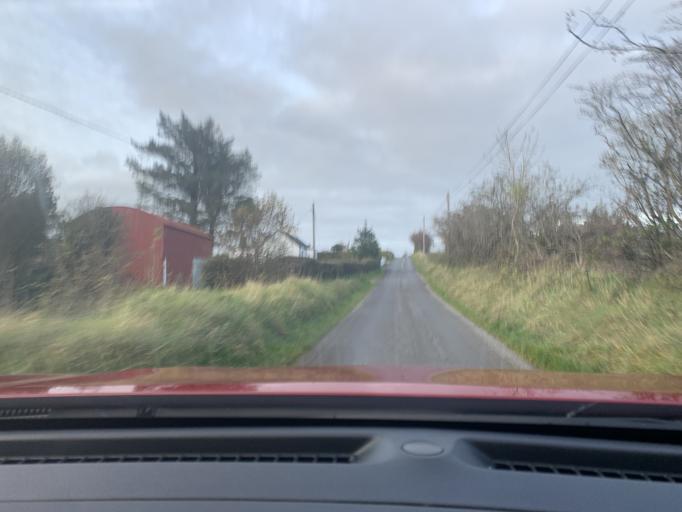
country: IE
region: Connaught
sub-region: Roscommon
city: Ballaghaderreen
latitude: 53.9770
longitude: -8.6191
